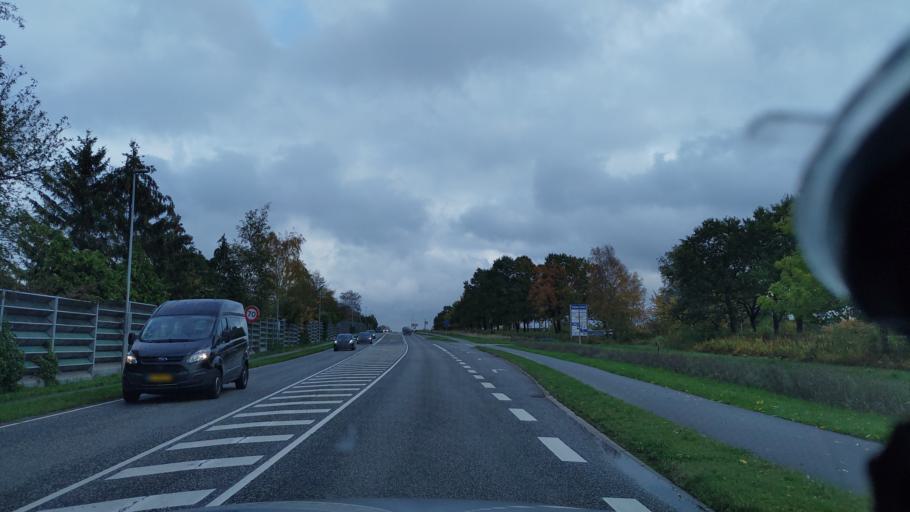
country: DK
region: Zealand
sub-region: Naestved Kommune
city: Naestved
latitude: 55.2501
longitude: 11.7726
